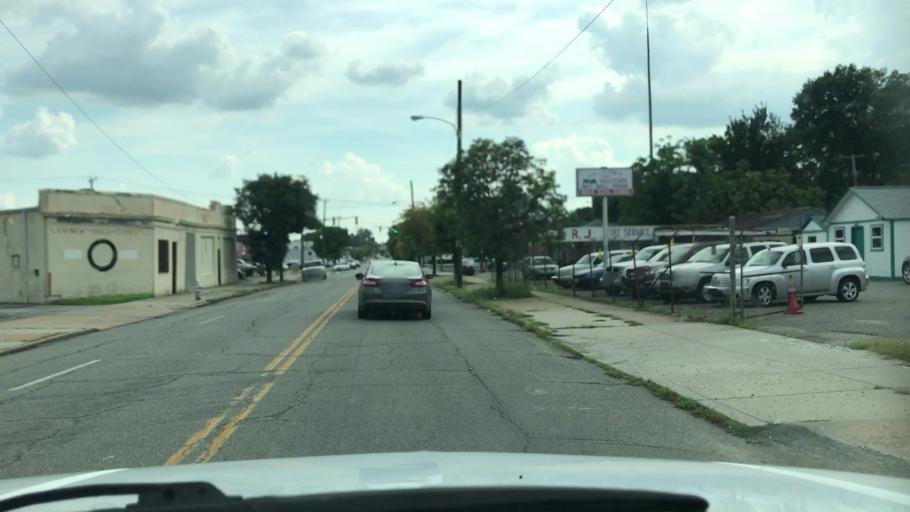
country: US
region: Virginia
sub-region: City of Richmond
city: Richmond
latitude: 37.5664
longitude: -77.4448
